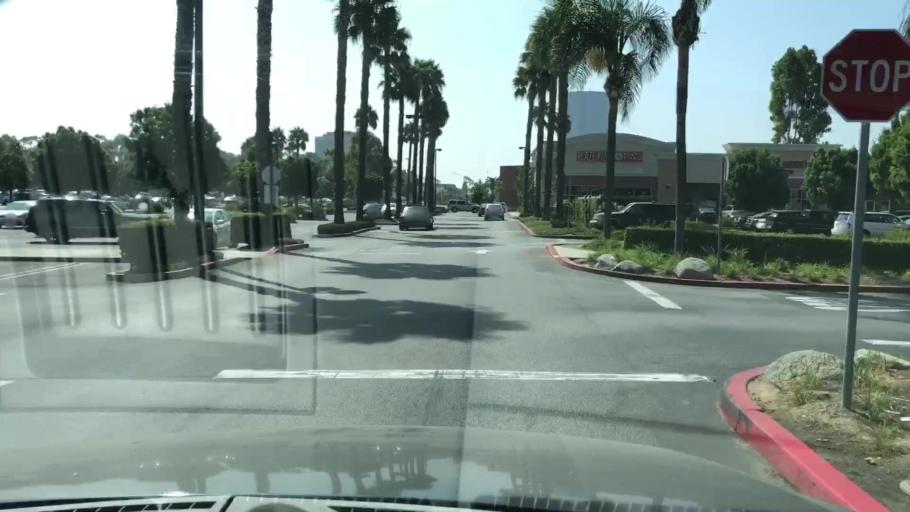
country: US
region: California
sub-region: Ventura County
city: El Rio
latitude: 34.2341
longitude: -119.1781
